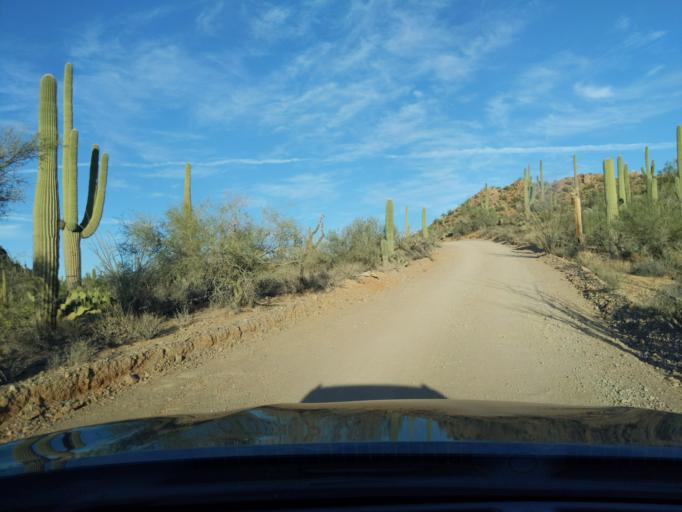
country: US
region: Arizona
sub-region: Pima County
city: Picture Rocks
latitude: 32.2795
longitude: -111.1942
